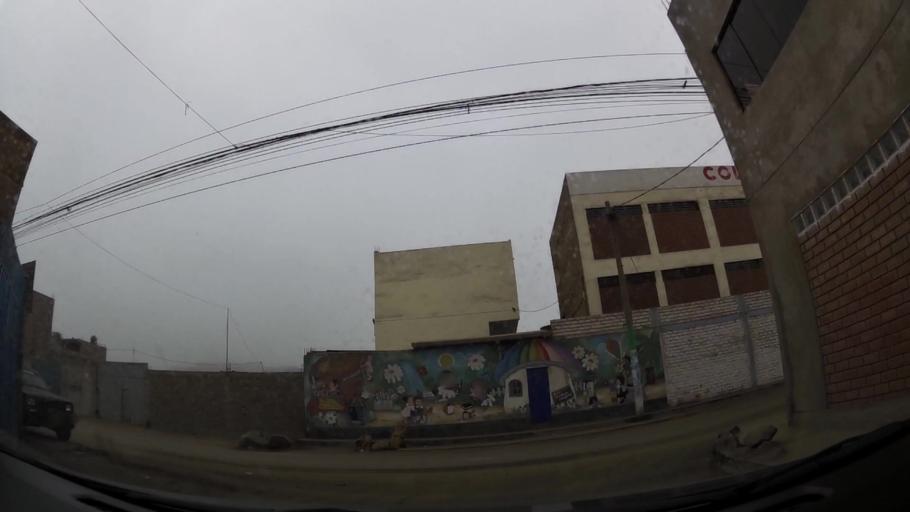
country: PE
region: Lima
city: Ventanilla
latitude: -11.8409
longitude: -77.1023
